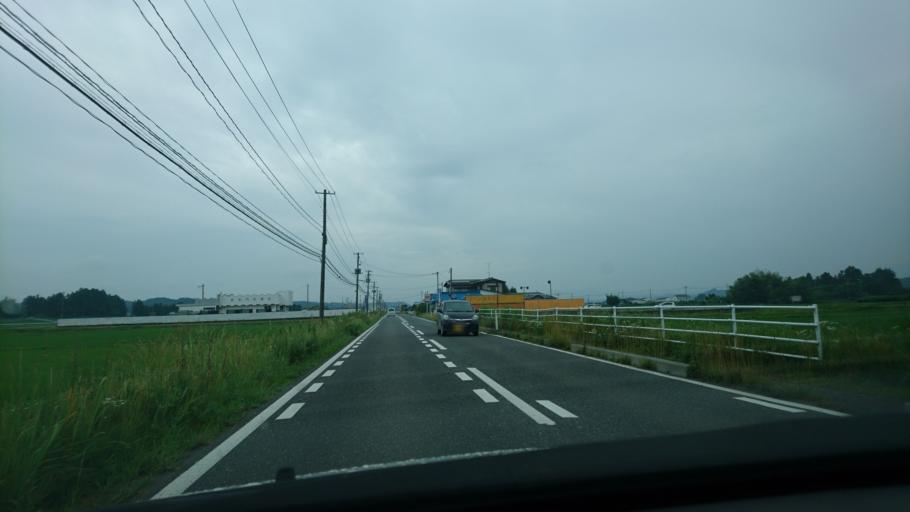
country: JP
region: Miyagi
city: Furukawa
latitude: 38.7324
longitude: 140.9693
